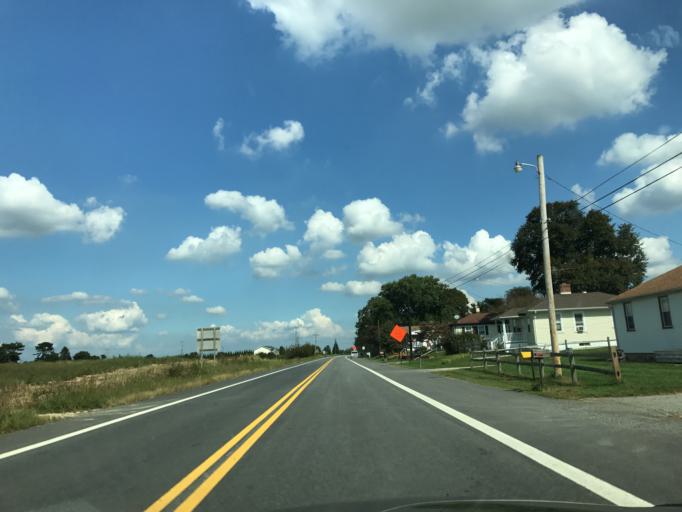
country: US
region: Delaware
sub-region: New Castle County
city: Middletown
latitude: 39.4207
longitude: -75.7724
